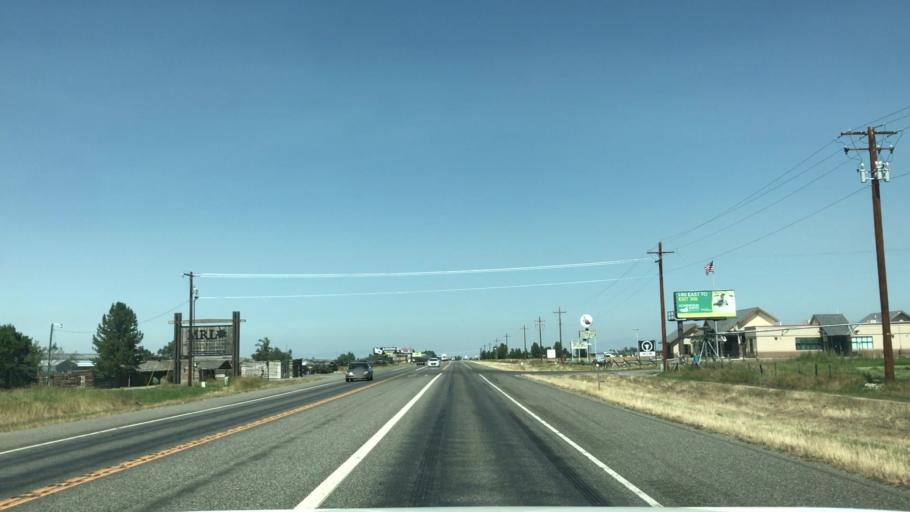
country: US
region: Montana
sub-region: Gallatin County
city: Four Corners
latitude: 45.5829
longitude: -111.1970
